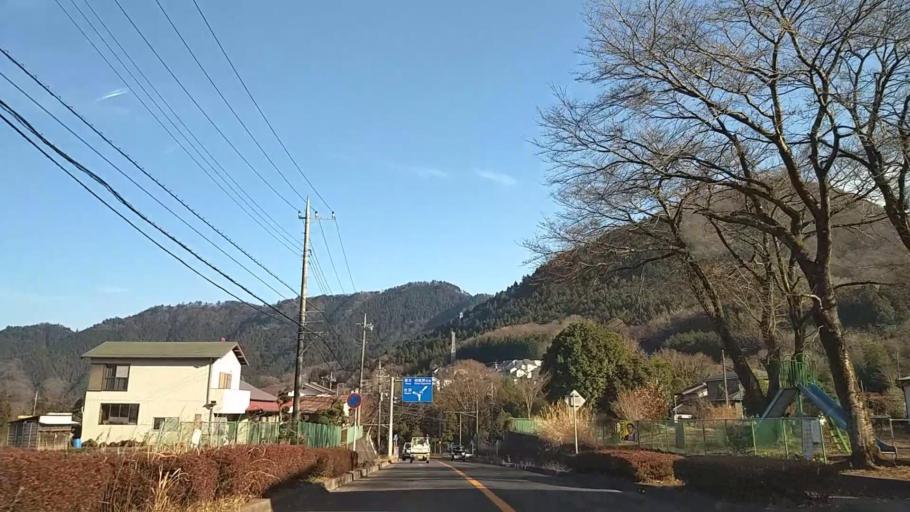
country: JP
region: Yamanashi
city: Uenohara
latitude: 35.5637
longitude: 139.2055
